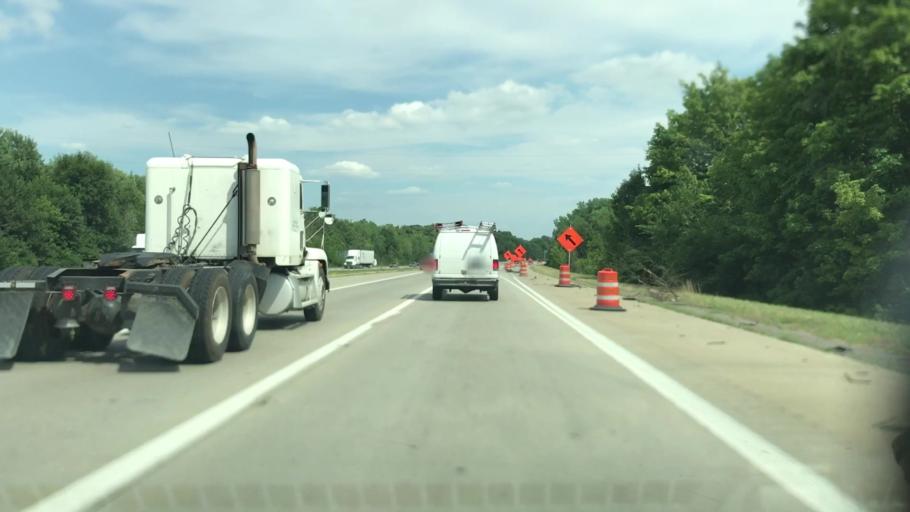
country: US
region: Ohio
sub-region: Franklin County
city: Grove City
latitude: 39.8993
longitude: -83.0541
